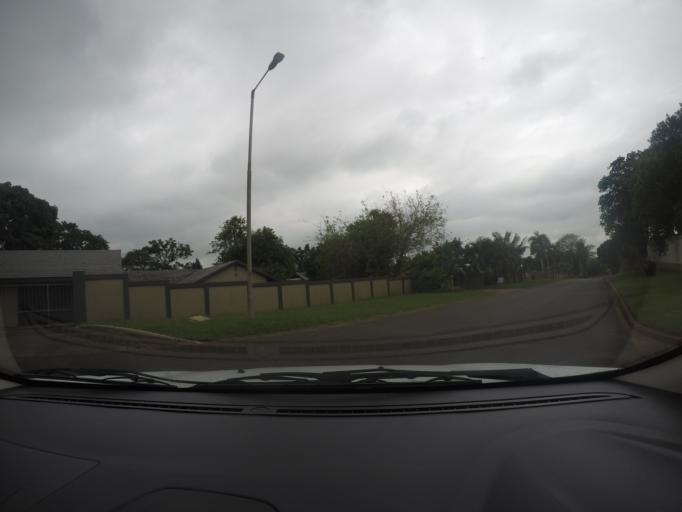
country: ZA
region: KwaZulu-Natal
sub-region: uThungulu District Municipality
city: Empangeni
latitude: -28.7609
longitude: 31.8945
